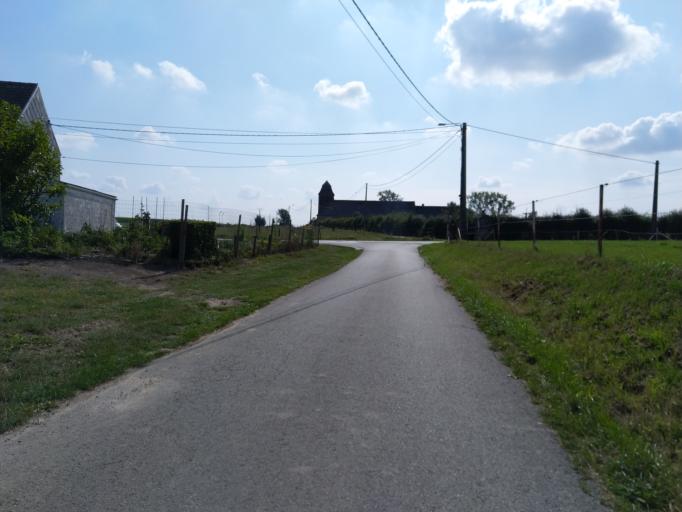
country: BE
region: Wallonia
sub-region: Province du Hainaut
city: Jurbise
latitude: 50.5555
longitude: 3.9789
